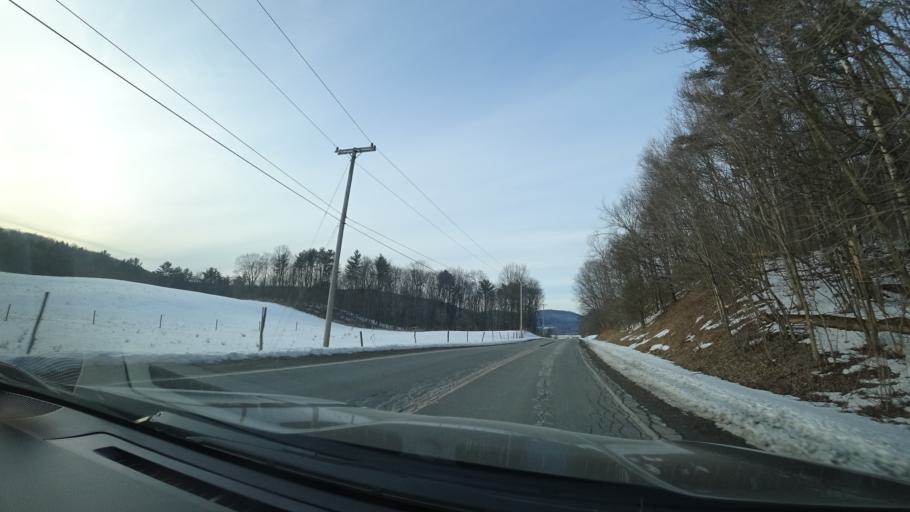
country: US
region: New York
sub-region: Washington County
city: Greenwich
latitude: 43.1904
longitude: -73.3765
